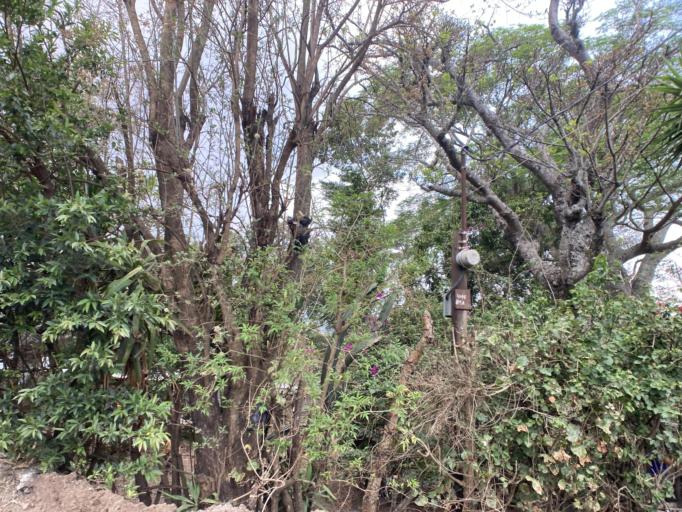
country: GT
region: Escuintla
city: San Vicente Pacaya
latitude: 14.3360
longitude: -90.5704
